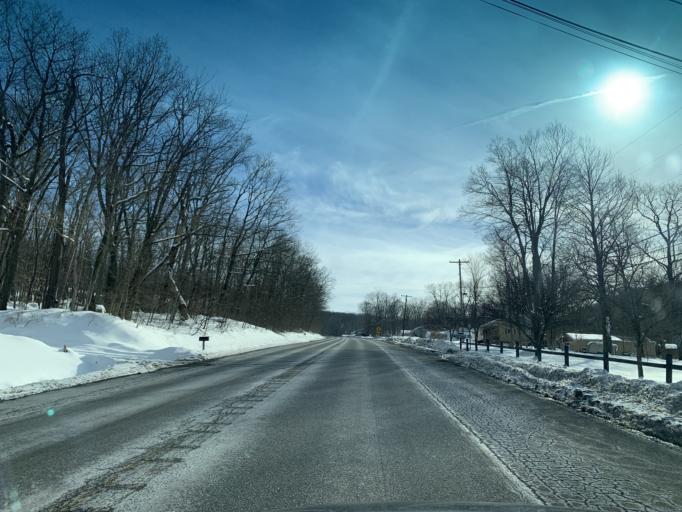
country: US
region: Maryland
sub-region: Allegany County
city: Frostburg
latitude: 39.6269
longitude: -78.8983
